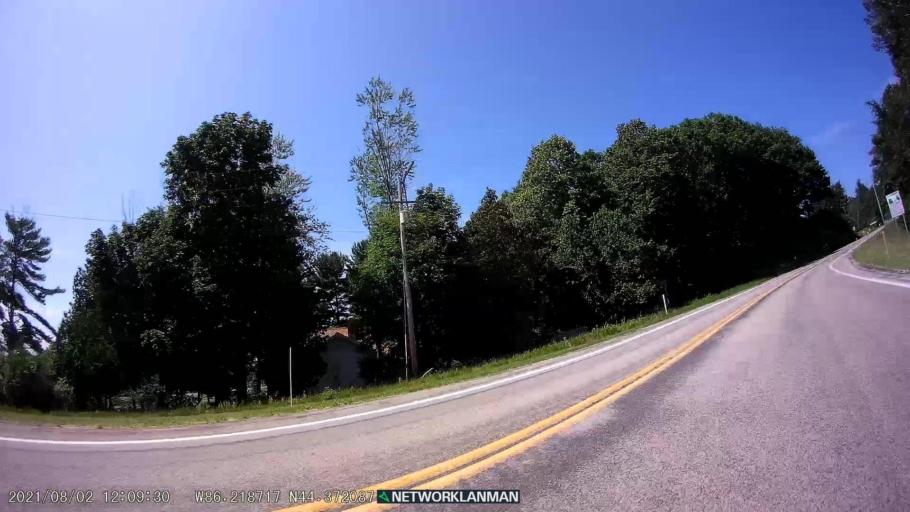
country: US
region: Michigan
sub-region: Manistee County
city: Manistee
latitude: 44.3724
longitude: -86.2186
